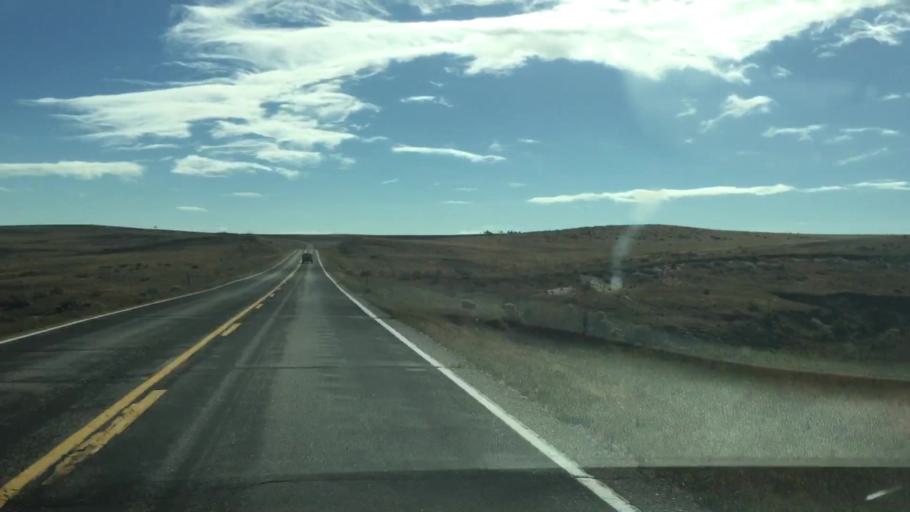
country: US
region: Colorado
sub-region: Elbert County
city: Kiowa
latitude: 39.2783
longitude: -104.2686
